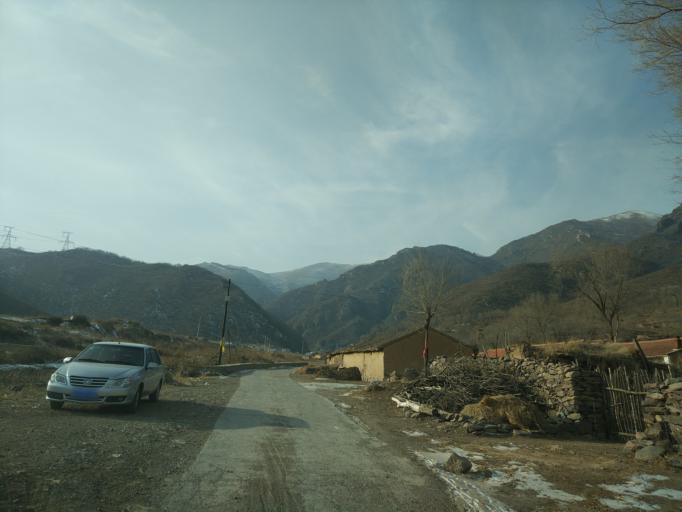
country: CN
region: Hebei
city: Xiwanzi
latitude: 40.8150
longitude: 115.4584
